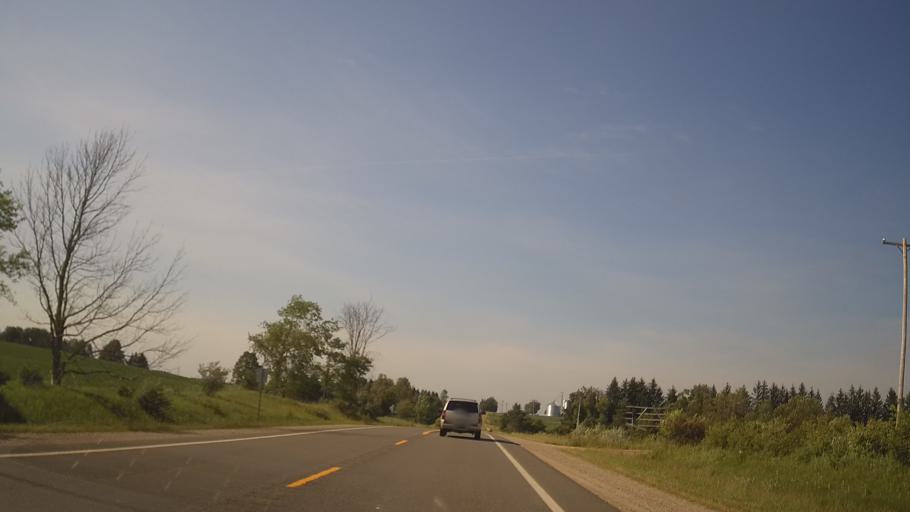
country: US
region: Michigan
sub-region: Ogemaw County
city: West Branch
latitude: 44.3507
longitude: -84.1259
